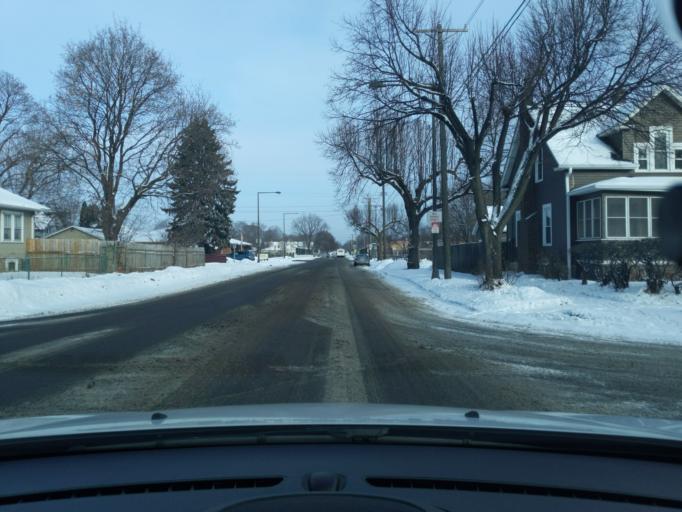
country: US
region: Minnesota
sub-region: Ramsey County
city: Saint Paul
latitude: 44.9502
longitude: -93.1365
